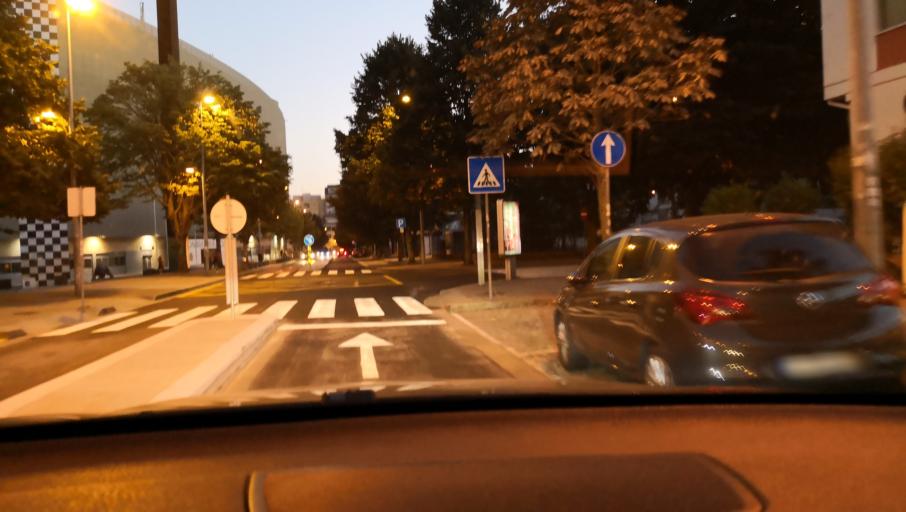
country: PT
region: Porto
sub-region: Matosinhos
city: Senhora da Hora
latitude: 41.1635
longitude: -8.6432
